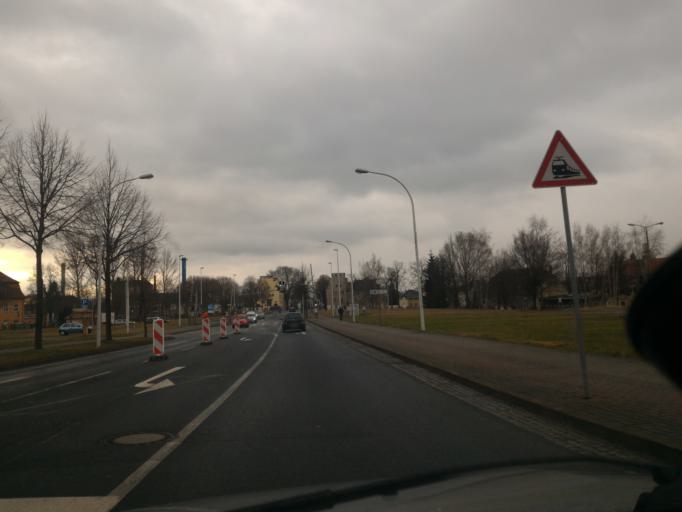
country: DE
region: Saxony
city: Zittau
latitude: 50.8903
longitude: 14.8119
